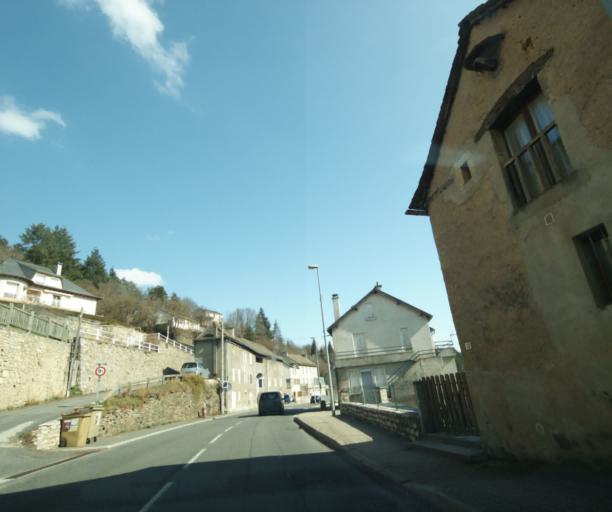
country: FR
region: Languedoc-Roussillon
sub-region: Departement de la Lozere
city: Mende
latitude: 44.5359
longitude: 3.5516
